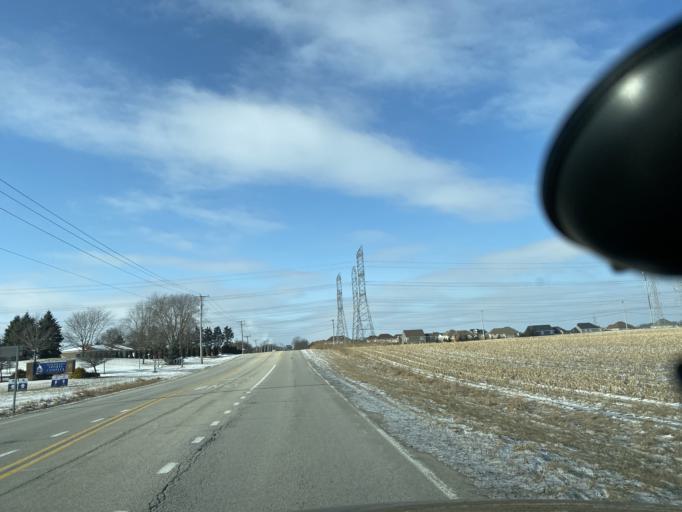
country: US
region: Illinois
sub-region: Will County
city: Goodings Grove
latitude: 41.6509
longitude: -87.9330
